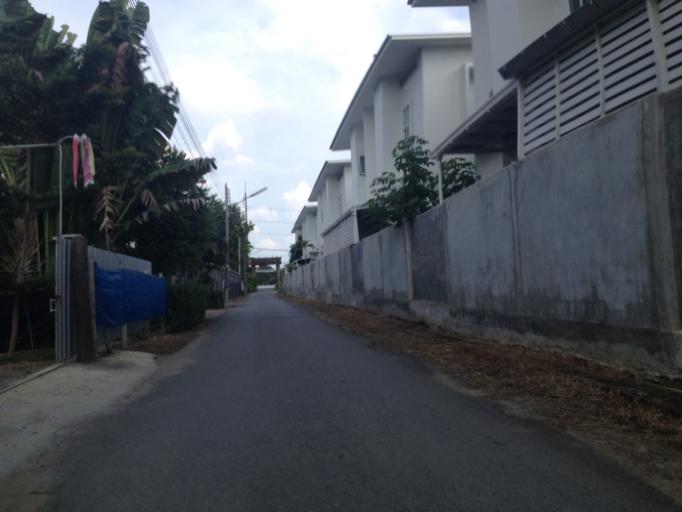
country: TH
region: Chiang Mai
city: Hang Dong
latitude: 18.7264
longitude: 98.9253
